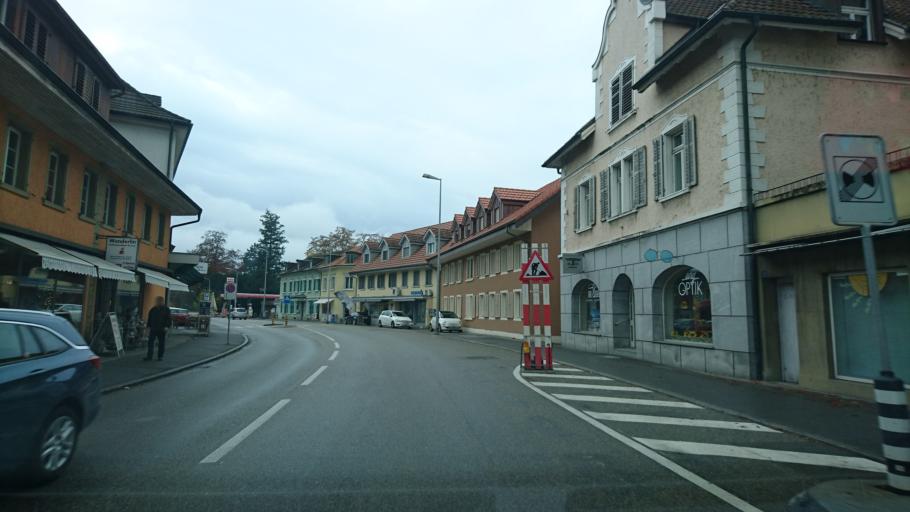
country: CH
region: Solothurn
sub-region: Bezirk Olten
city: Schonenwerd
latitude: 47.3699
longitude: 8.0014
